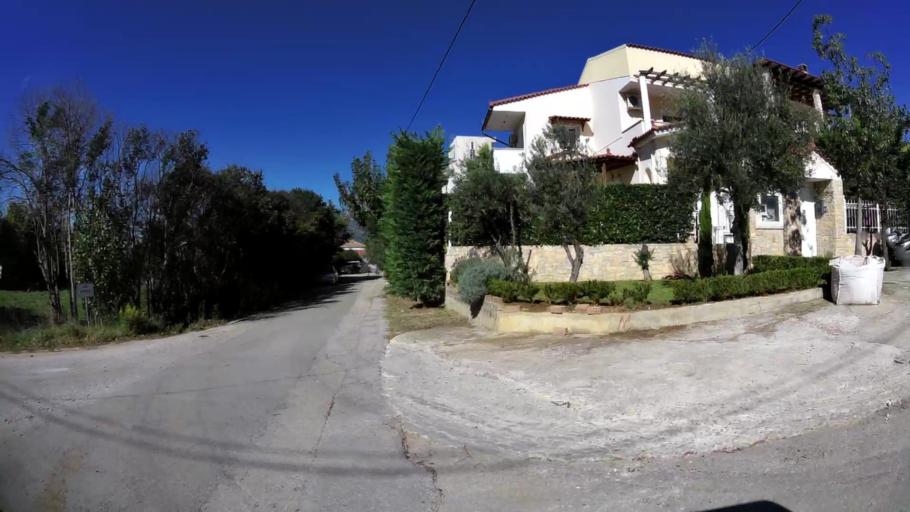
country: GR
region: Attica
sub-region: Nomarchia Athinas
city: Lykovrysi
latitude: 38.0934
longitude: 23.7859
